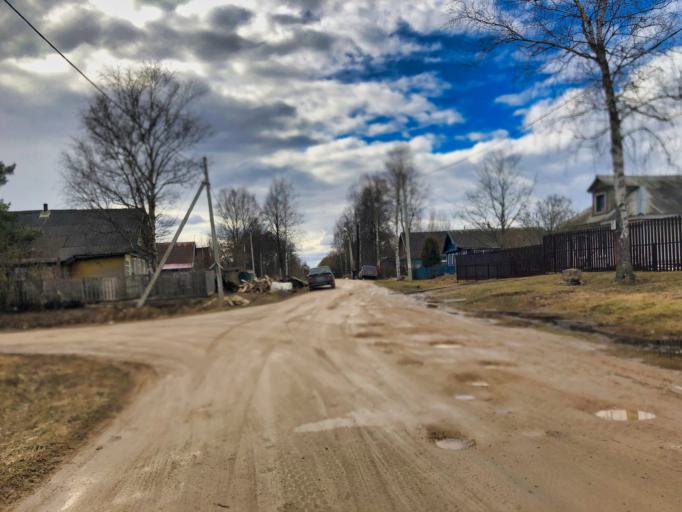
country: RU
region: Tverskaya
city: Rzhev
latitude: 56.2257
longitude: 34.3062
